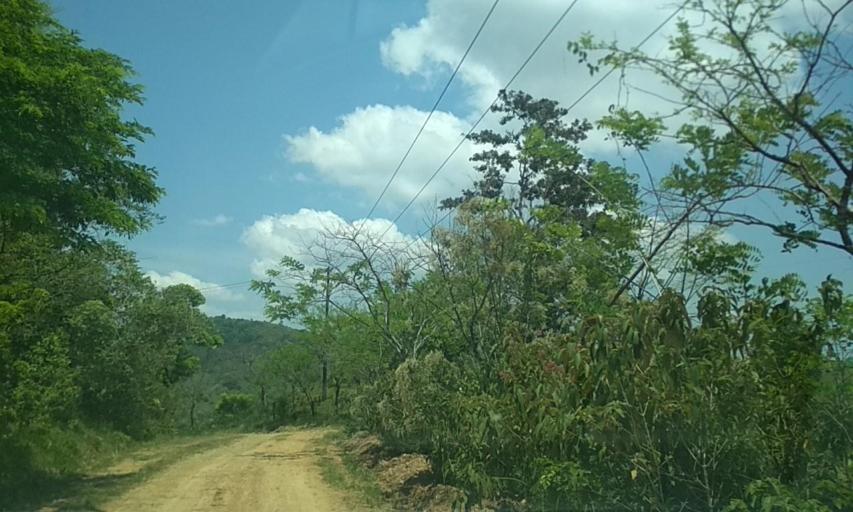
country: MX
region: Chiapas
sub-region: Tecpatan
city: Raudales Malpaso
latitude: 17.3993
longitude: -93.7477
